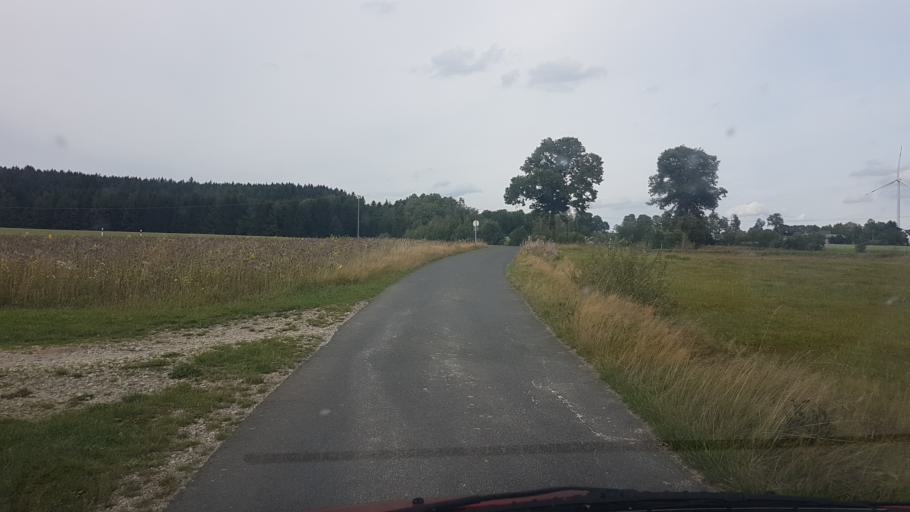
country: DE
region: Bavaria
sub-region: Upper Franconia
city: Hochstadt bei Thiersheim
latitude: 50.0751
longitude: 12.0681
